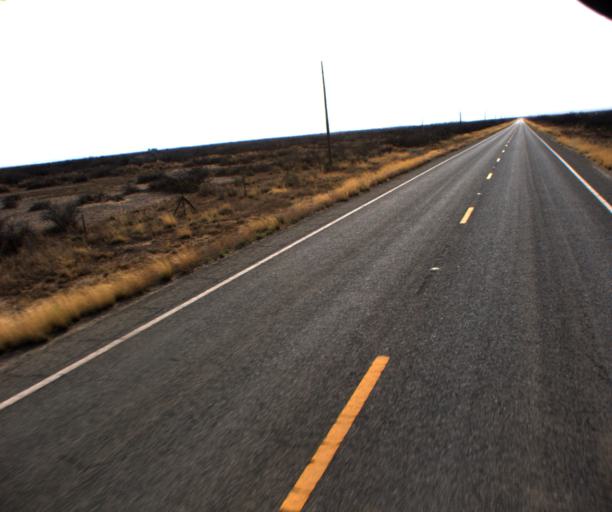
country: US
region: Arizona
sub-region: Cochise County
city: Willcox
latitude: 32.1953
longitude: -109.7286
